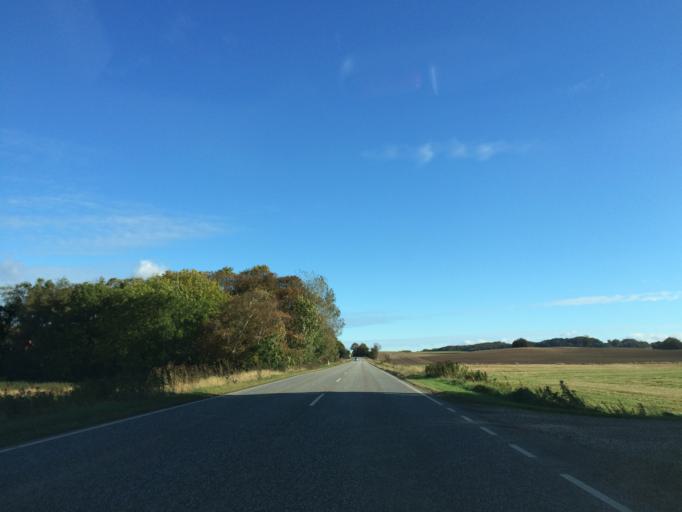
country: DK
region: Central Jutland
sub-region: Randers Kommune
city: Langa
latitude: 56.3769
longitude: 9.9467
